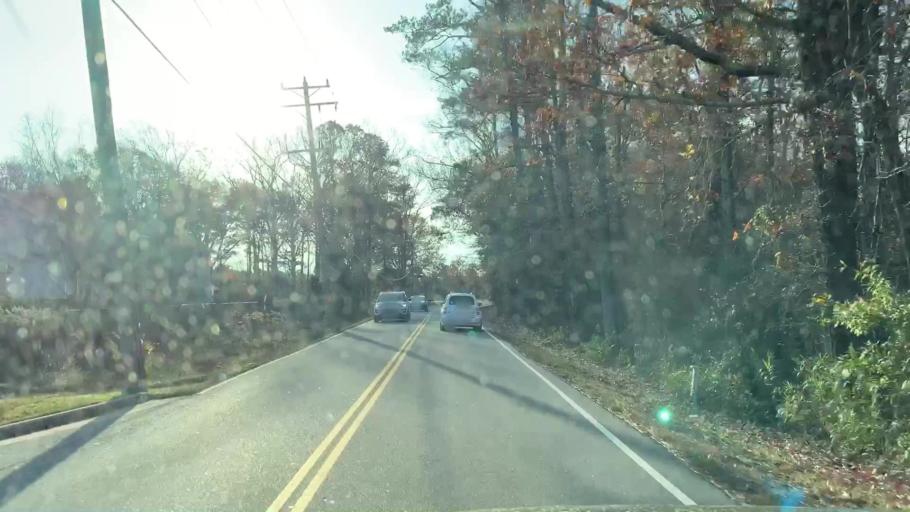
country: US
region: Virginia
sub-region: City of Chesapeake
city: Chesapeake
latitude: 36.7669
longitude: -76.1503
